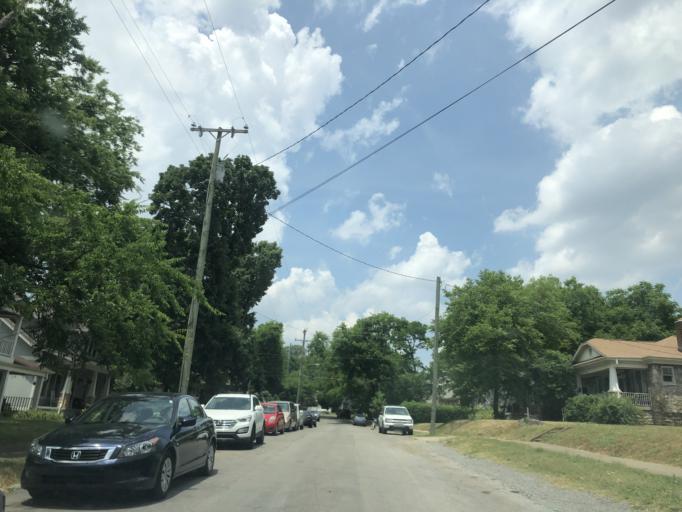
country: US
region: Tennessee
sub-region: Davidson County
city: Nashville
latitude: 36.1292
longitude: -86.8136
